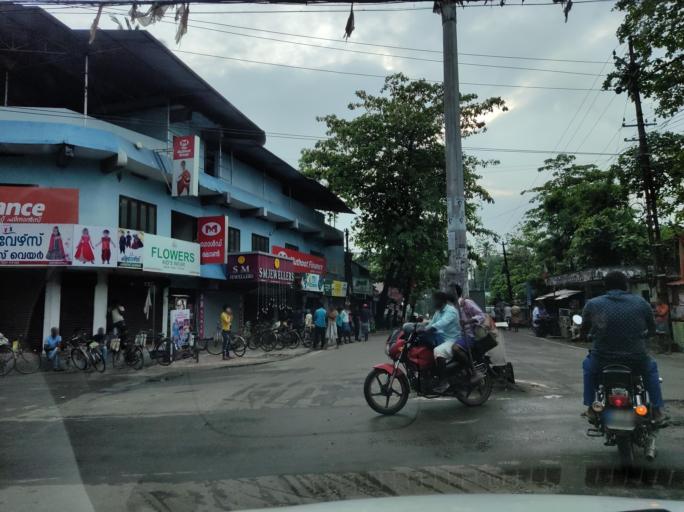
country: IN
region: Kerala
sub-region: Alappuzha
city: Kayankulam
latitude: 9.2603
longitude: 76.4498
